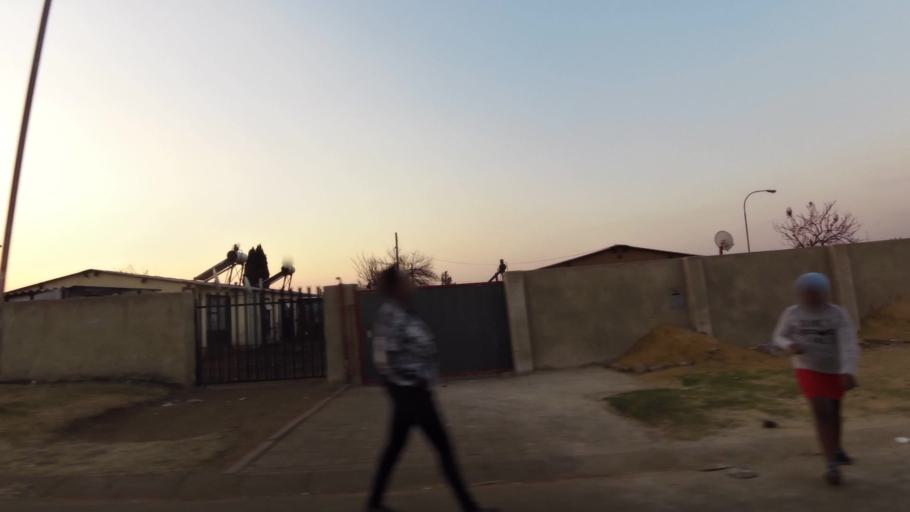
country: ZA
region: Gauteng
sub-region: City of Johannesburg Metropolitan Municipality
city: Soweto
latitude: -26.2859
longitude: 27.8813
